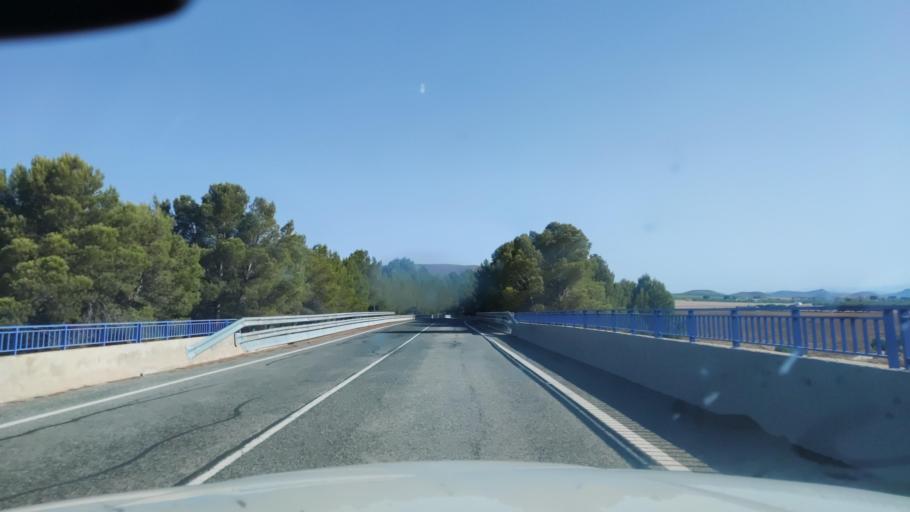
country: ES
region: Castille-La Mancha
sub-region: Provincia de Albacete
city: Tobarra
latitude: 38.6401
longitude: -1.6677
